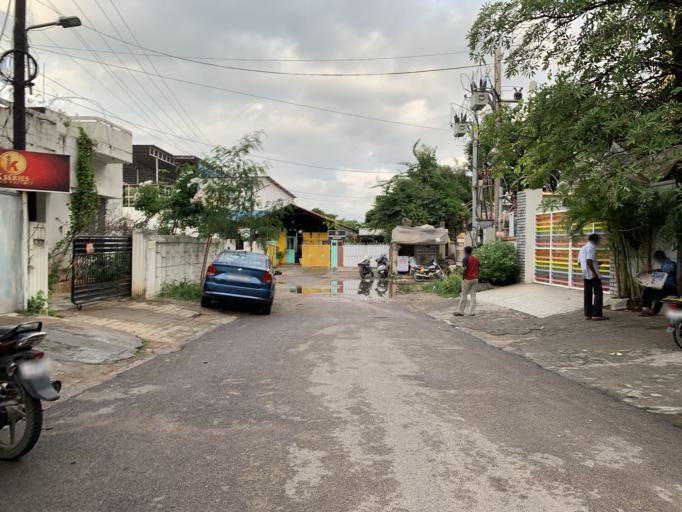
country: IN
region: Telangana
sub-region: Hyderabad
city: Hyderabad
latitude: 17.4266
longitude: 78.4348
